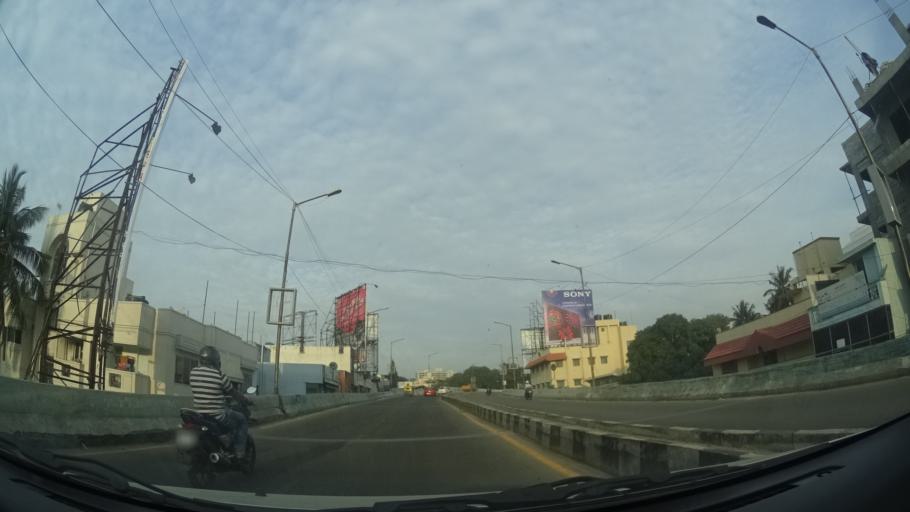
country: IN
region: Karnataka
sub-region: Bangalore Urban
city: Bangalore
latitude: 12.9970
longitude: 77.6229
